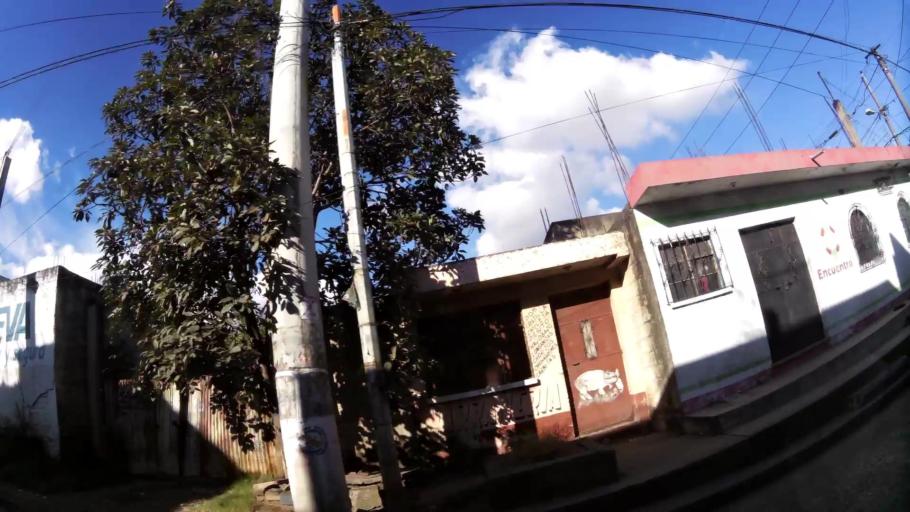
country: GT
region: Guatemala
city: Villa Nueva
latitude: 14.5231
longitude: -90.5795
